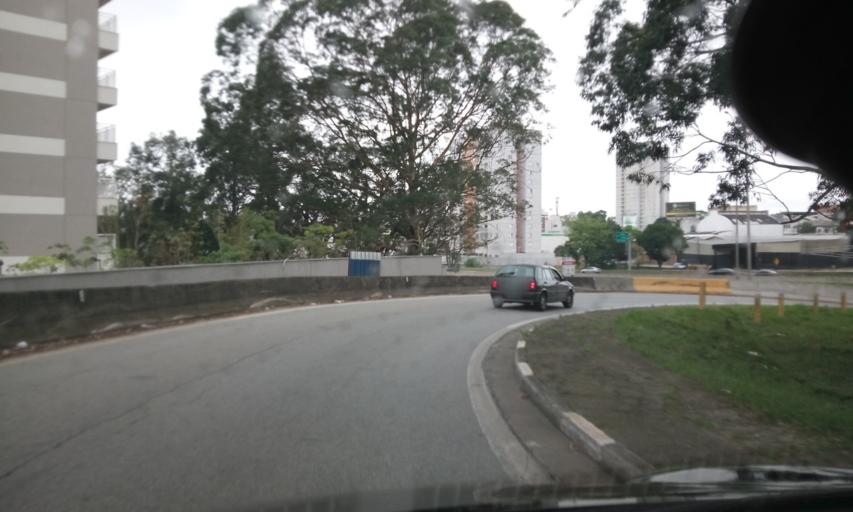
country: BR
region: Sao Paulo
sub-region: Sao Bernardo Do Campo
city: Sao Bernardo do Campo
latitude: -23.6900
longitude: -46.5638
